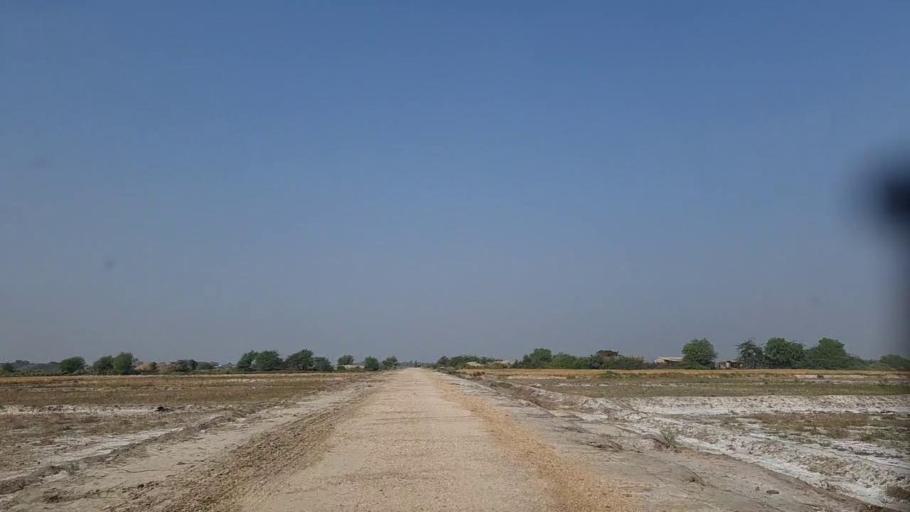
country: PK
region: Sindh
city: Mirpur Batoro
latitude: 24.5845
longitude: 68.1366
